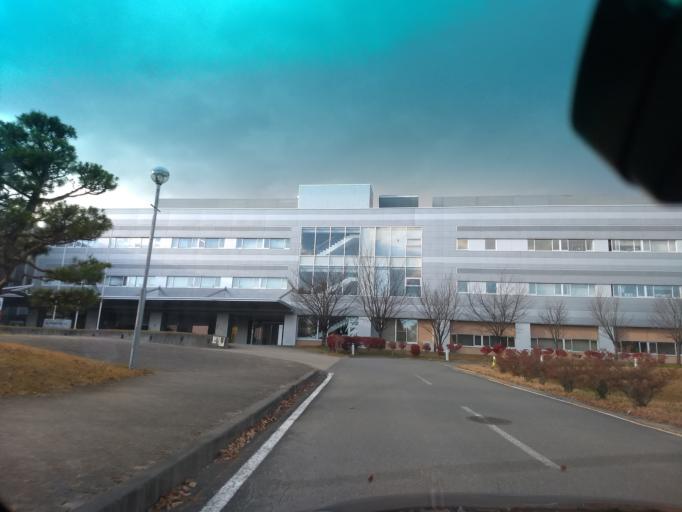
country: JP
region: Nagano
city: Chino
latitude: 36.0080
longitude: 138.1852
